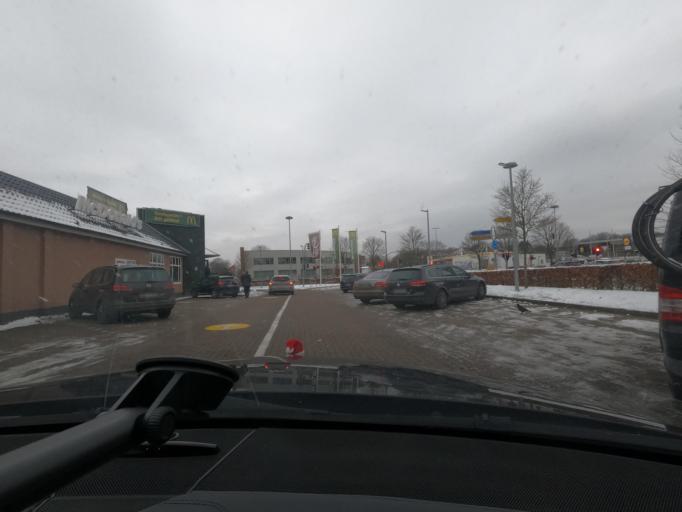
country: DE
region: Schleswig-Holstein
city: Flensburg
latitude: 54.7767
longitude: 9.4145
